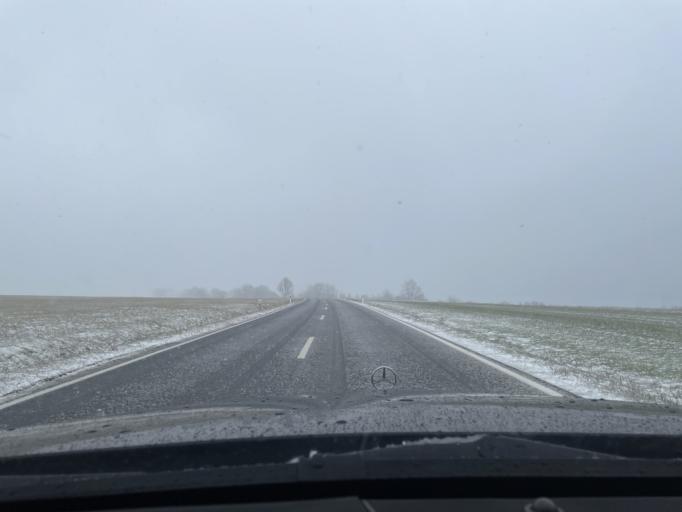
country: DE
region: Thuringia
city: Effelder
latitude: 51.2358
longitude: 10.2547
